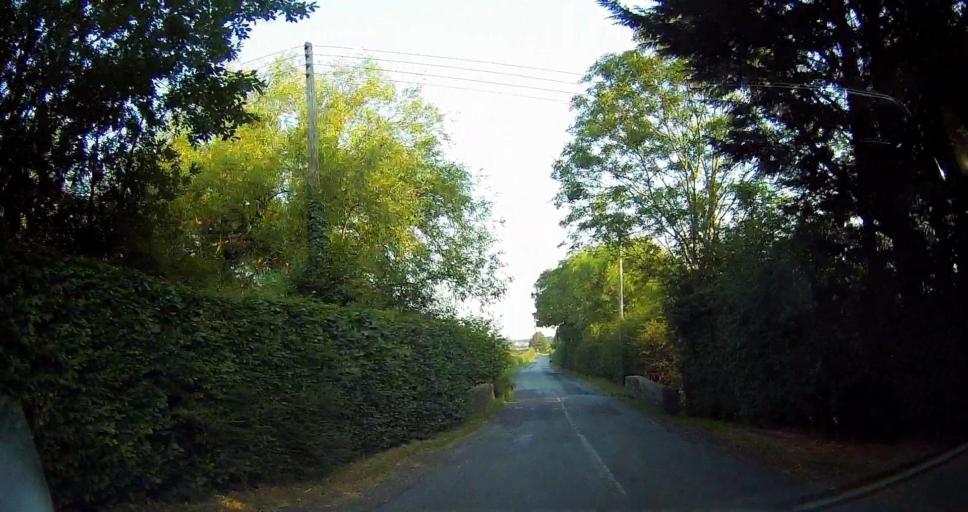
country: GB
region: England
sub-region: Cheshire East
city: Nantwich
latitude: 53.0502
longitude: -2.5231
